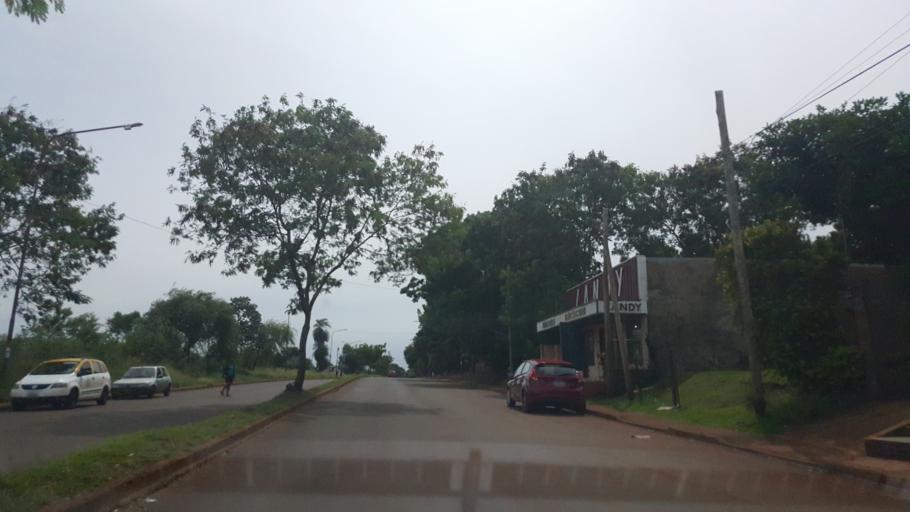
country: AR
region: Misiones
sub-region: Departamento de Capital
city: Posadas
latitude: -27.3822
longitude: -55.9414
